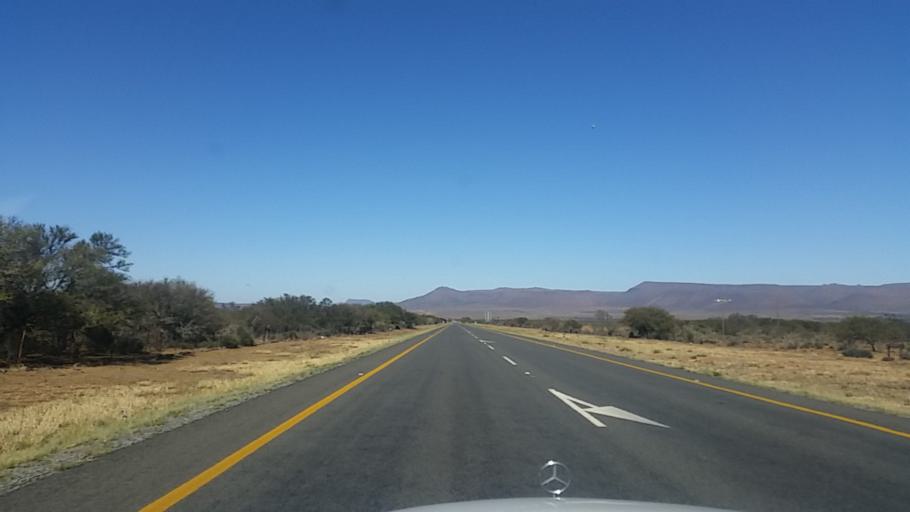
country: ZA
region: Eastern Cape
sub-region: Cacadu District Municipality
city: Graaff-Reinet
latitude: -31.9809
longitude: 24.7000
